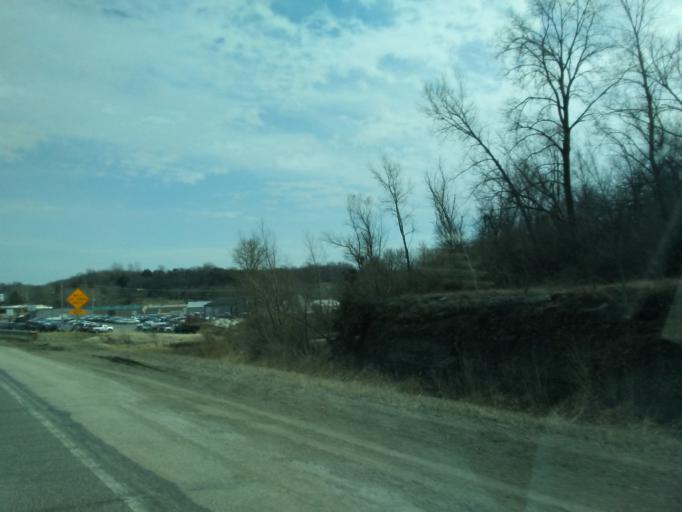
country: US
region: Iowa
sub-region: Winneshiek County
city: Decorah
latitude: 43.2899
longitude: -91.7607
